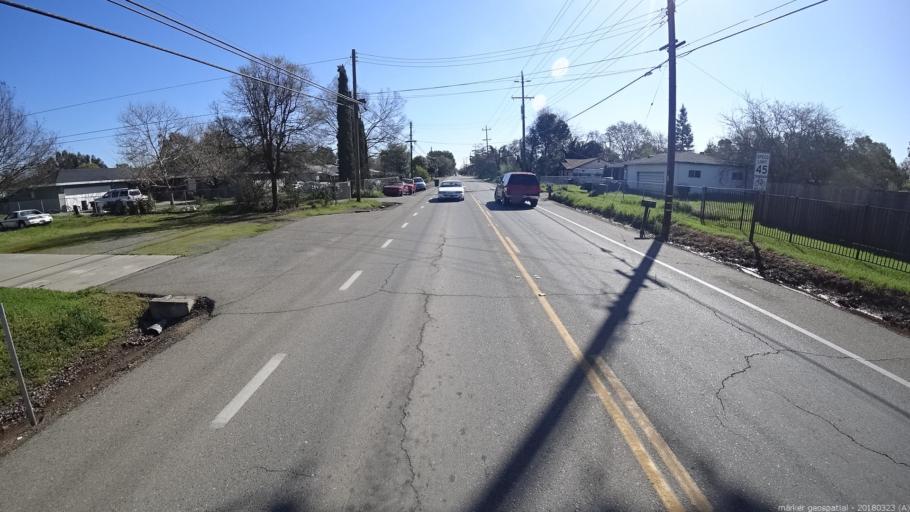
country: US
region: California
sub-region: Sacramento County
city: Rio Linda
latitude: 38.6982
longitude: -121.4380
